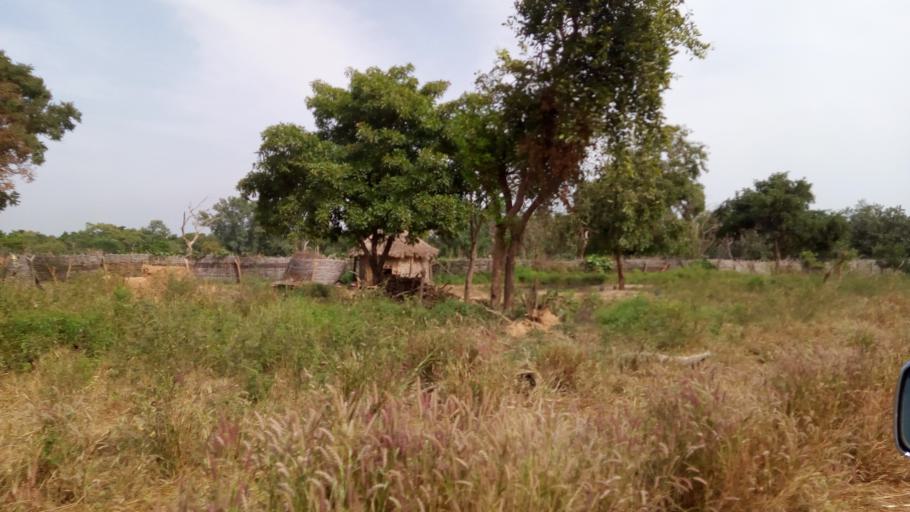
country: ML
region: Kayes
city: Kita
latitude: 13.2595
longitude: -8.8534
